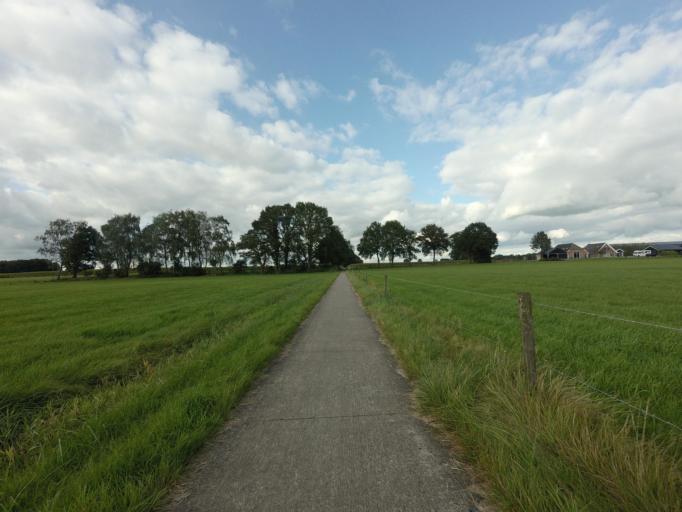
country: NL
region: Overijssel
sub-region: Gemeente Deventer
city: Schalkhaar
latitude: 52.2692
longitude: 6.2622
